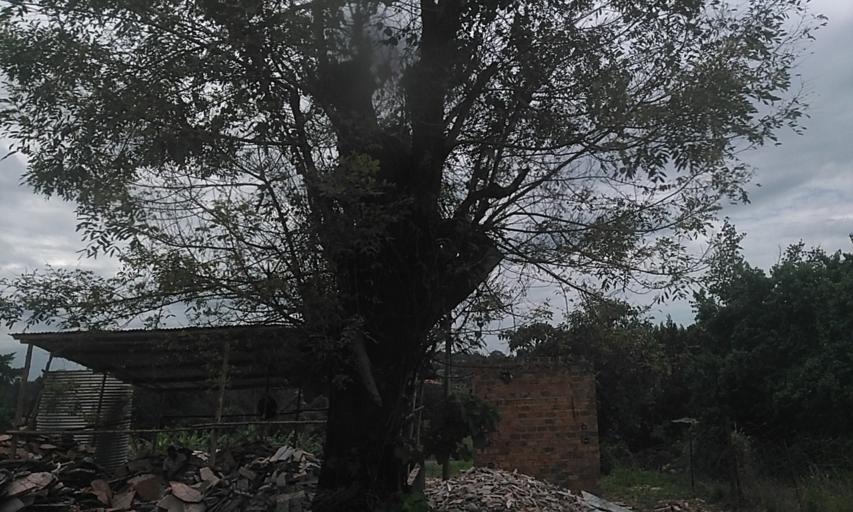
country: UG
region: Central Region
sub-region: Wakiso District
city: Bweyogerere
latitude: 0.3947
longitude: 32.6880
